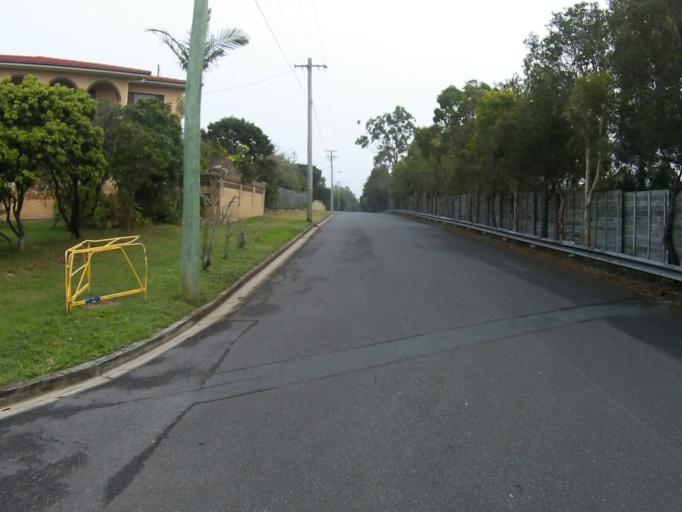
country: AU
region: Queensland
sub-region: Brisbane
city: Nathan
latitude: -27.5556
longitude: 153.0710
